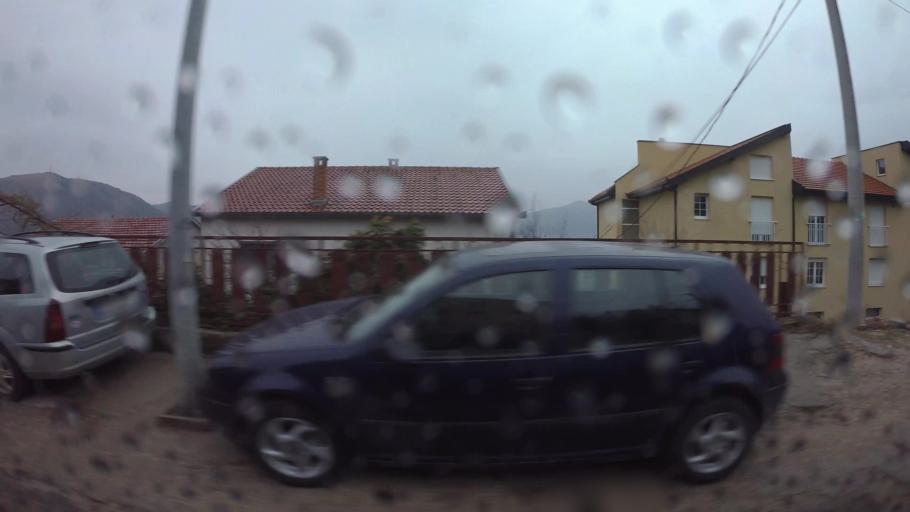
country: BA
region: Federation of Bosnia and Herzegovina
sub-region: Hercegovacko-Bosanski Kanton
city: Mostar
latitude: 43.3503
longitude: 17.8163
